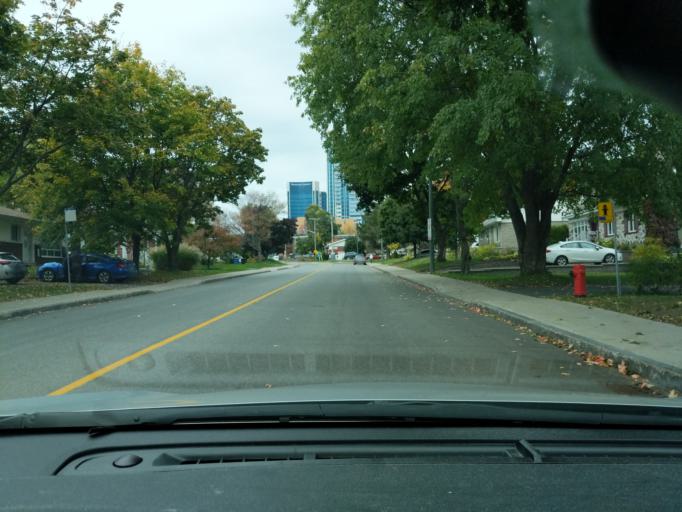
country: CA
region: Quebec
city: L'Ancienne-Lorette
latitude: 46.7644
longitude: -71.2844
